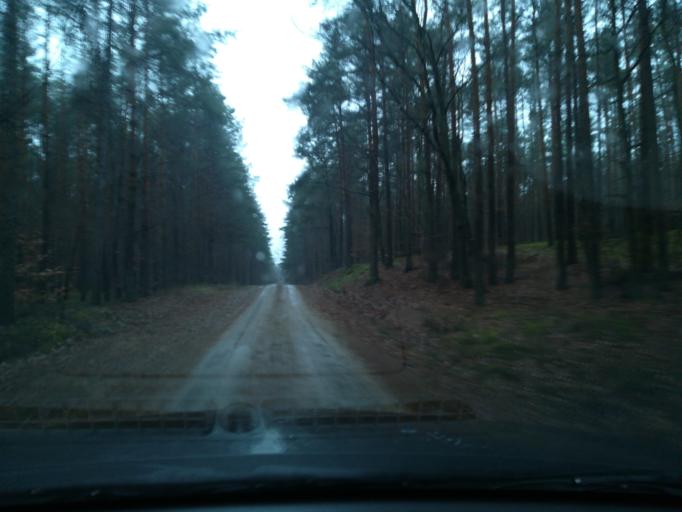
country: PL
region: Subcarpathian Voivodeship
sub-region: Powiat lancucki
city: Bialobrzegi
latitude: 50.1325
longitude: 22.3576
